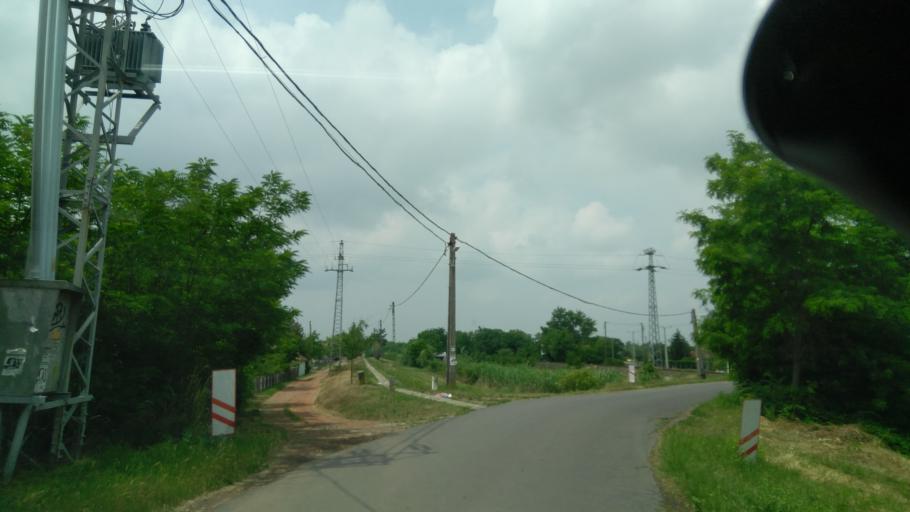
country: HU
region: Bekes
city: Gyula
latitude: 46.6567
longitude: 21.2584
